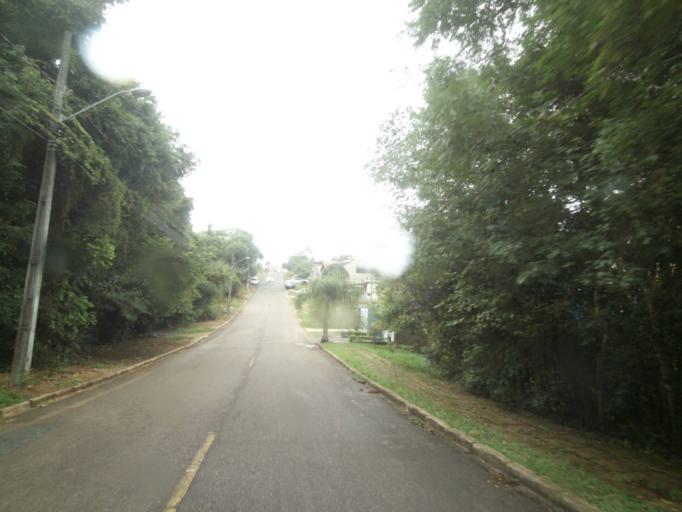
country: BR
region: Parana
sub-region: Curitiba
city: Curitiba
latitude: -25.4493
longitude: -49.3442
